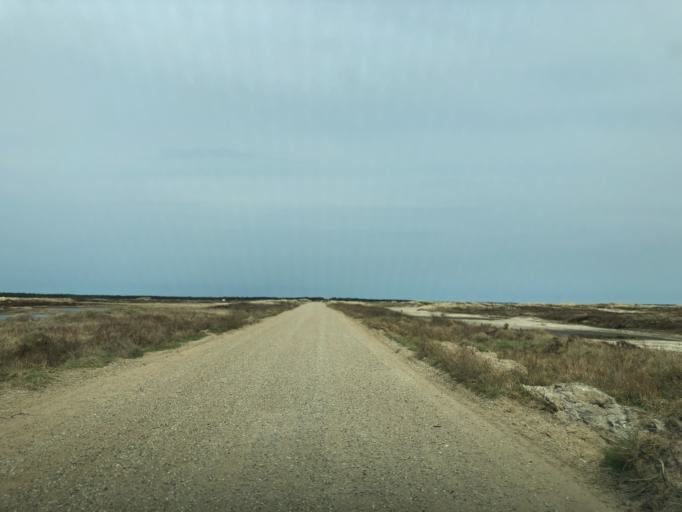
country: DK
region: South Denmark
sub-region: Varde Kommune
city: Oksbol
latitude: 55.5805
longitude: 8.1434
